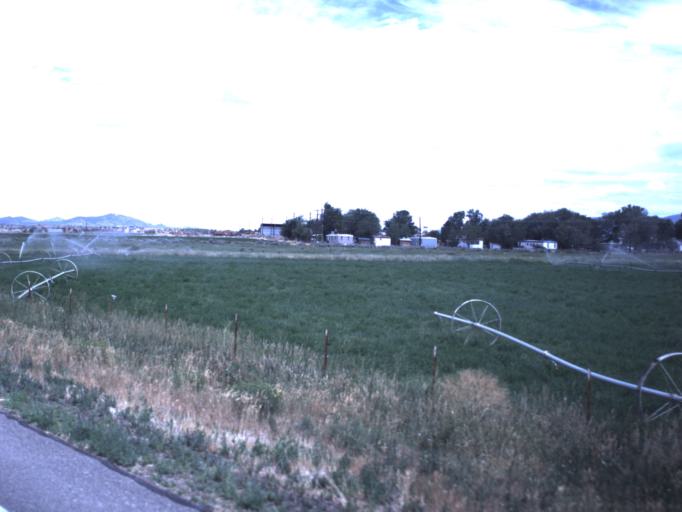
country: US
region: Utah
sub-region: Beaver County
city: Beaver
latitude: 38.2915
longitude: -112.6420
